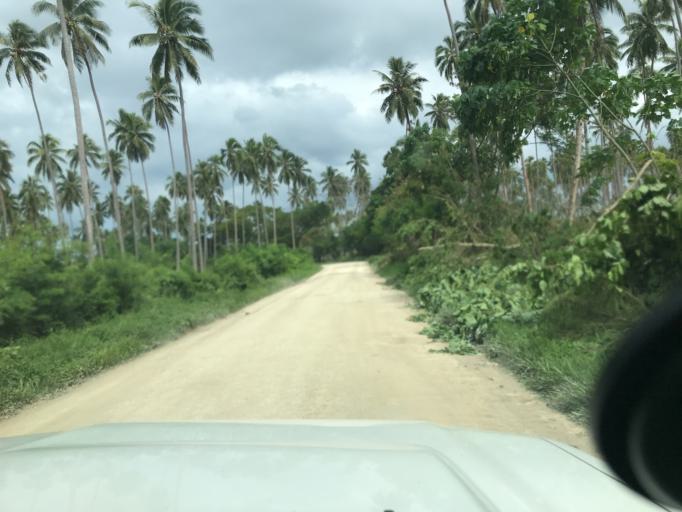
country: VU
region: Sanma
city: Luganville
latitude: -15.5907
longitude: 167.1126
